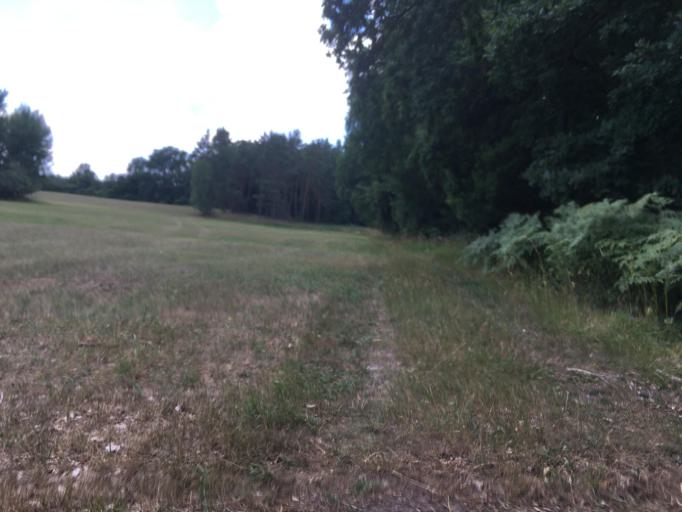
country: DE
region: Brandenburg
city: Althuttendorf
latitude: 52.9560
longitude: 13.7824
